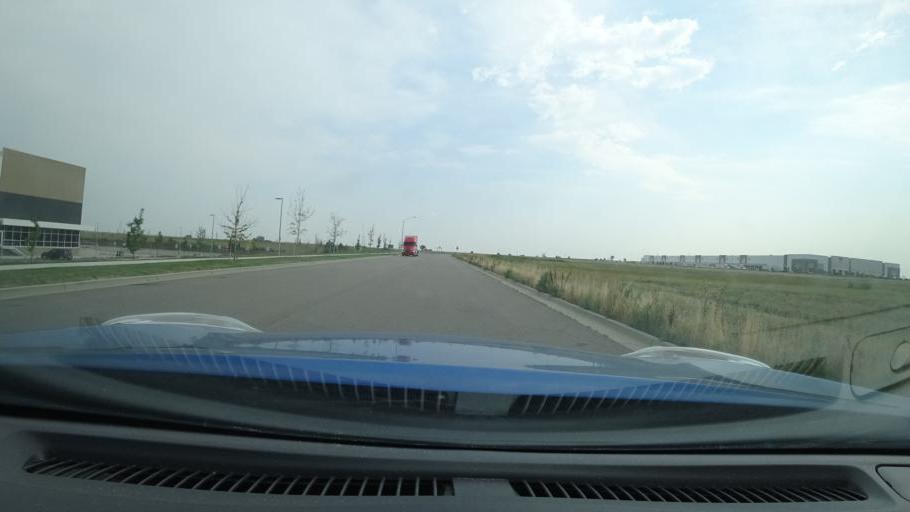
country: US
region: Colorado
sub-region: Adams County
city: Aurora
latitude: 39.7462
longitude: -104.7298
